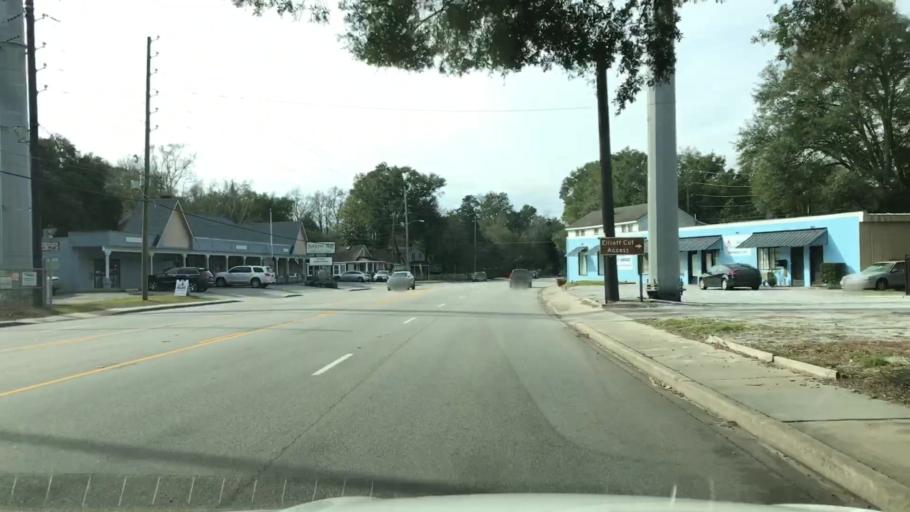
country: US
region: South Carolina
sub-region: Charleston County
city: Charleston
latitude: 32.7613
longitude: -79.9897
